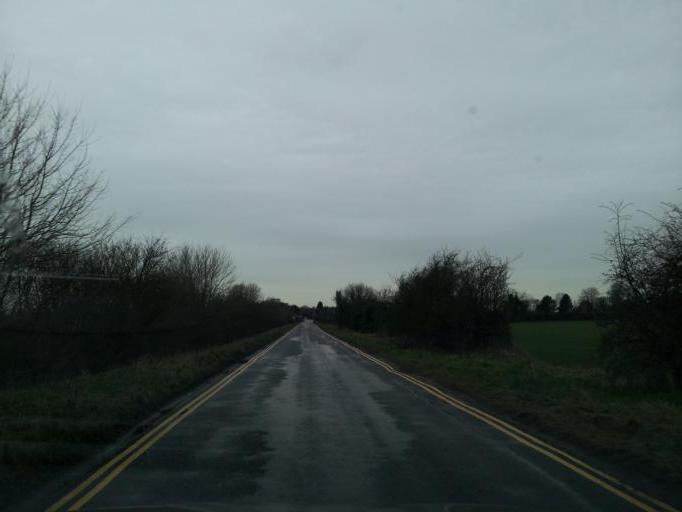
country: GB
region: England
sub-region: Cambridgeshire
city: Cambridge
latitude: 52.1730
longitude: 0.1580
